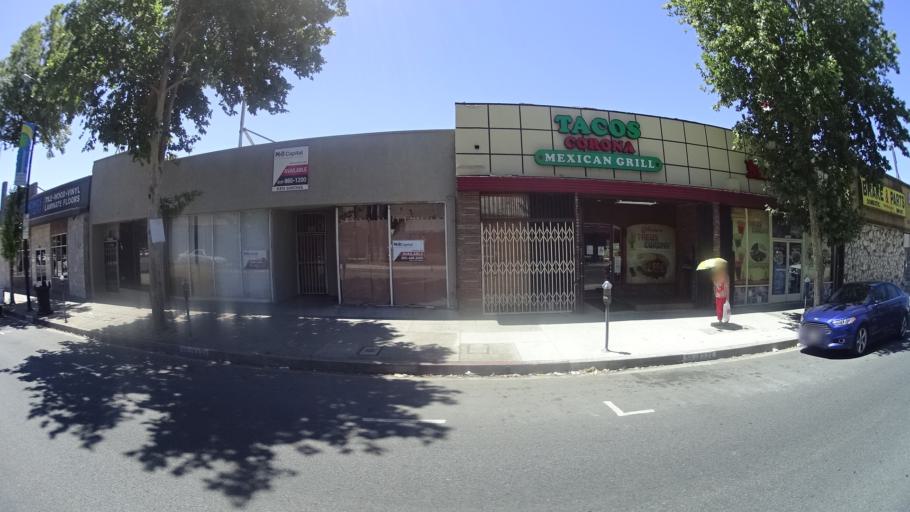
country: US
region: California
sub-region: Los Angeles County
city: Northridge
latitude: 34.2011
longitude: -118.5328
